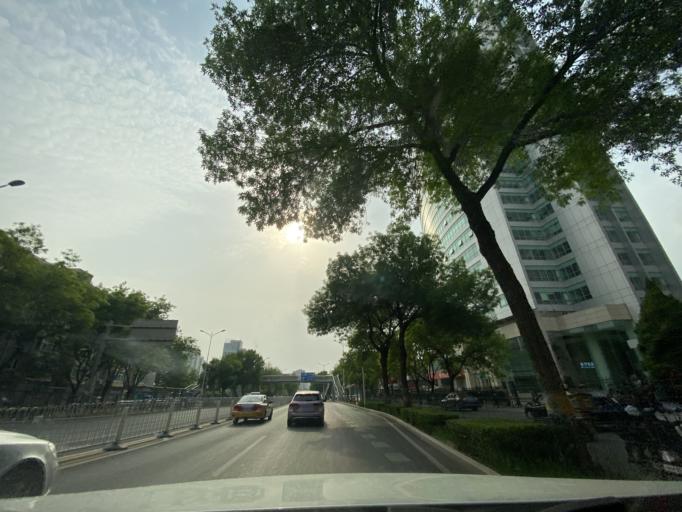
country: CN
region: Beijing
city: Haidian
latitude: 39.9752
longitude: 116.3389
